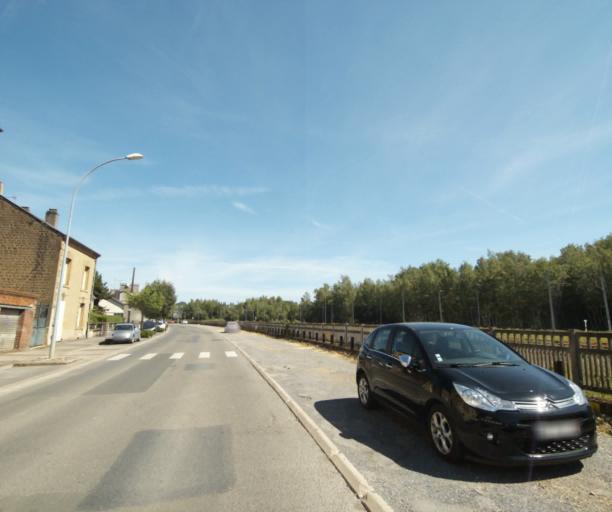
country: FR
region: Champagne-Ardenne
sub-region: Departement des Ardennes
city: Villers-Semeuse
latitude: 49.7475
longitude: 4.7363
